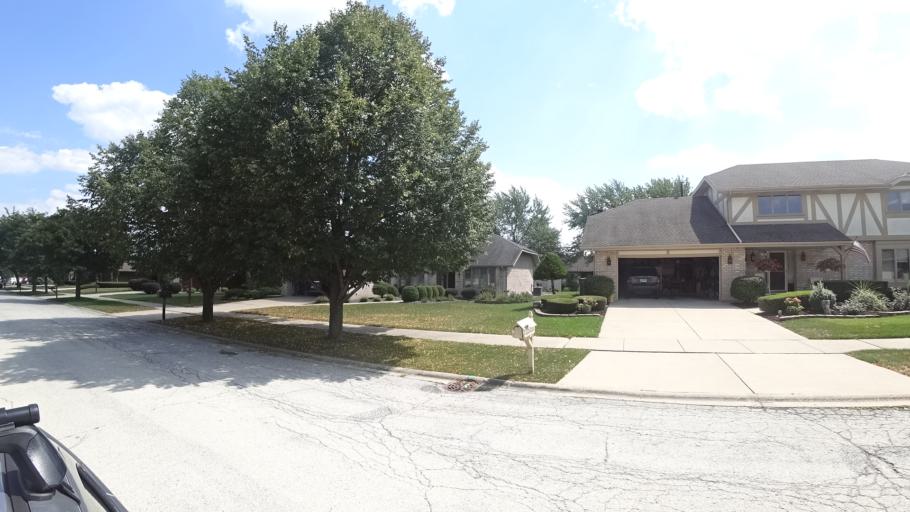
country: US
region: Illinois
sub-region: Cook County
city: Orland Park
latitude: 41.6304
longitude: -87.8224
